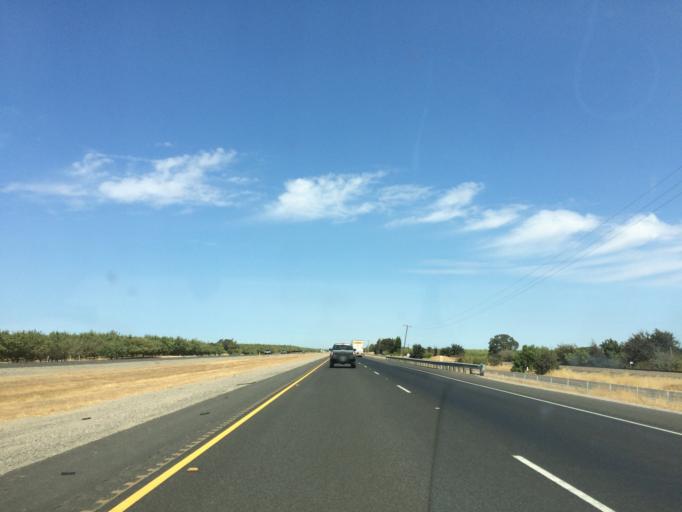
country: US
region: California
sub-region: Colusa County
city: Arbuckle
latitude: 38.9837
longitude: -122.0350
